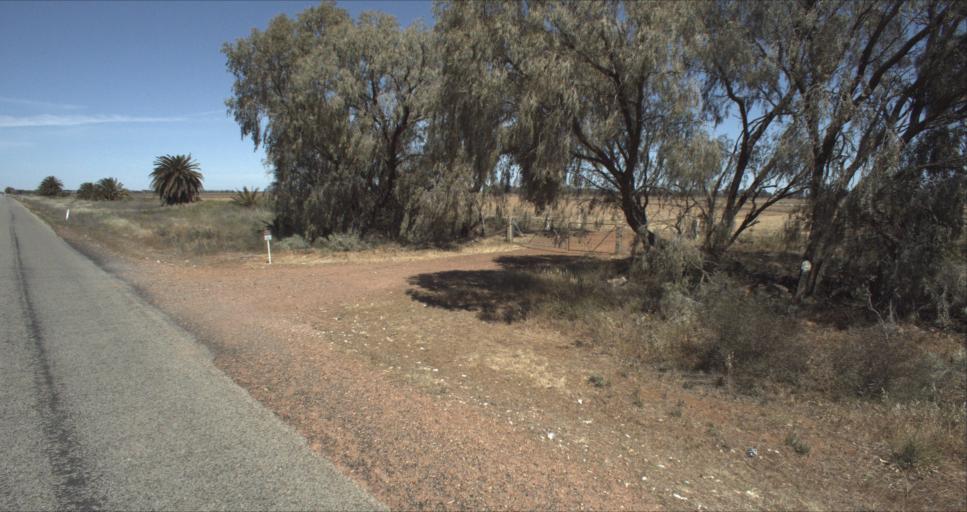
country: AU
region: New South Wales
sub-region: Leeton
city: Leeton
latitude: -34.4488
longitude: 146.2964
